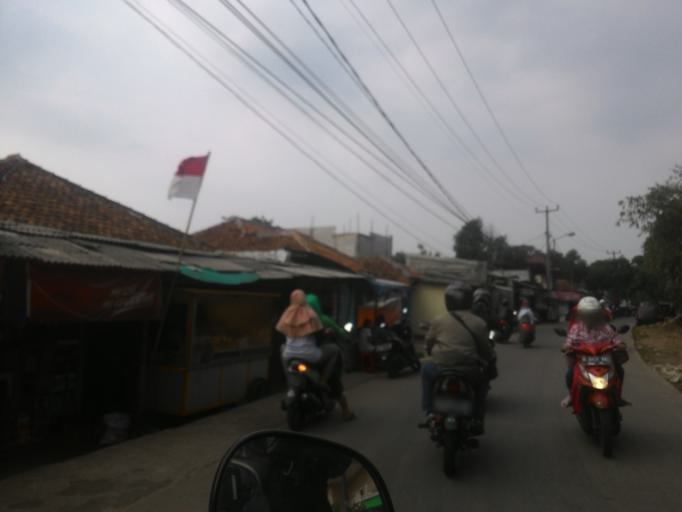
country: ID
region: West Java
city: Cibinong
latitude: -6.4530
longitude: 106.8396
